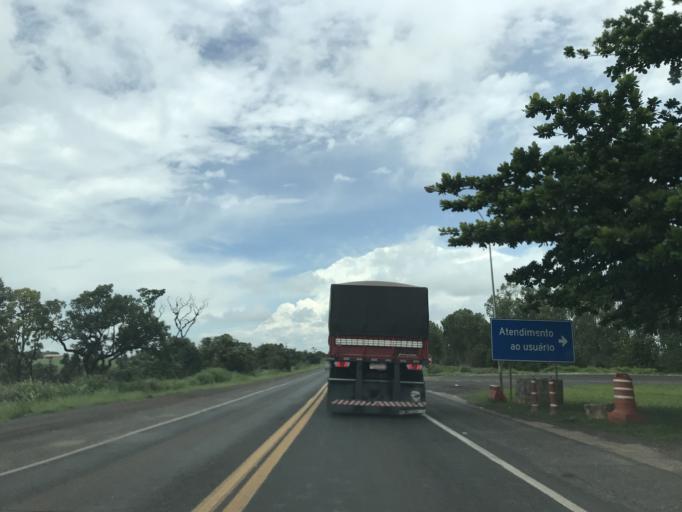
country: BR
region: Minas Gerais
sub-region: Frutal
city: Frutal
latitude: -19.7563
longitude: -48.9676
